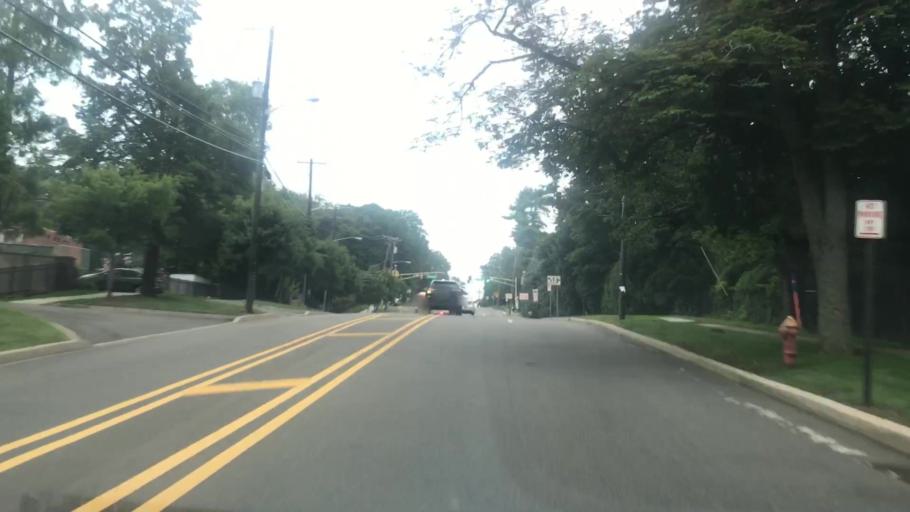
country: US
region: New Jersey
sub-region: Bergen County
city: Englewood Cliffs
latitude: 40.8870
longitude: -73.9627
